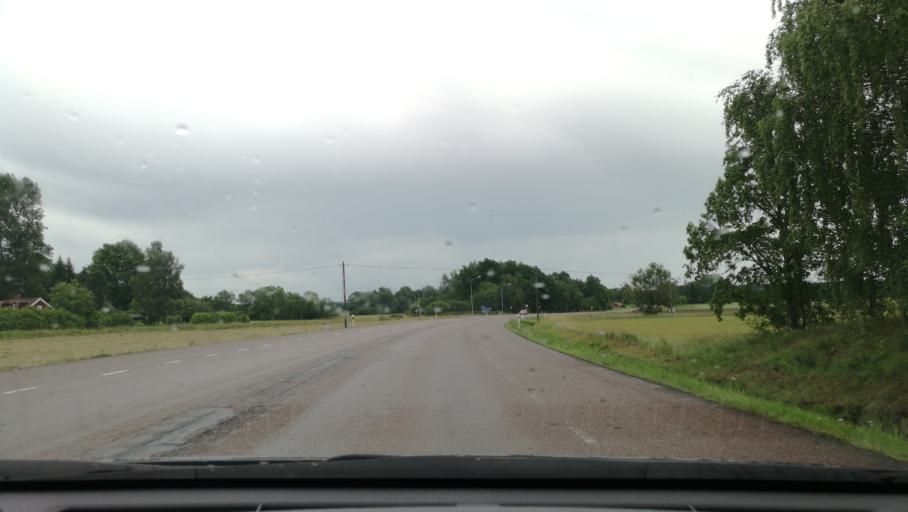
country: SE
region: Vaestmanland
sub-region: Kungsors Kommun
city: Kungsoer
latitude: 59.4478
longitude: 16.0416
